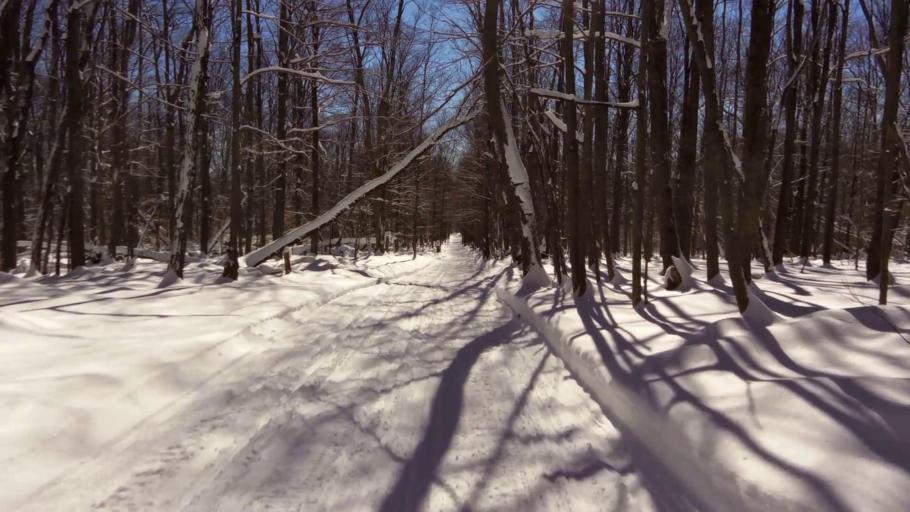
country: US
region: New York
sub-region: Chautauqua County
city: Mayville
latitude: 42.2091
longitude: -79.5348
